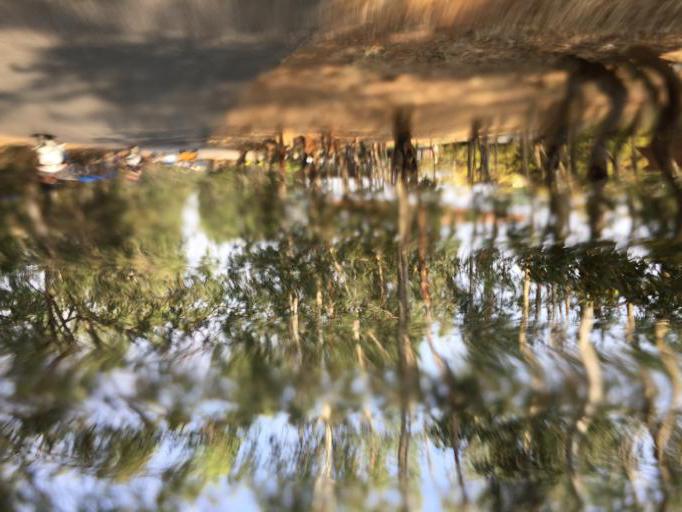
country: IN
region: Karnataka
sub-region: Chikkaballapur
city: Chik Ballapur
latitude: 13.3485
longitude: 77.6680
